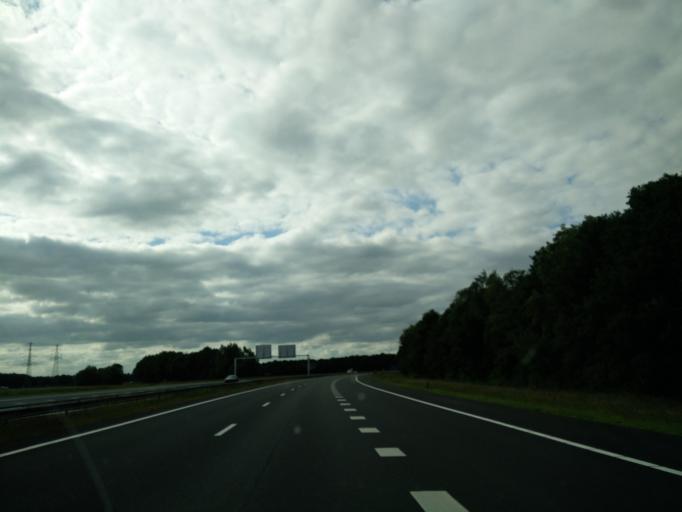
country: NL
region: Drenthe
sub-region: Gemeente Assen
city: Assen
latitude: 52.9783
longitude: 6.5315
